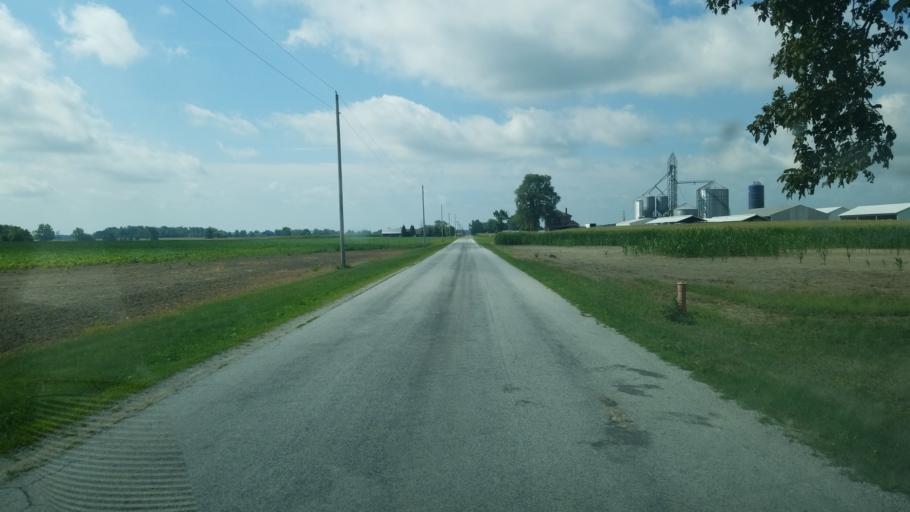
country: US
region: Ohio
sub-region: Hardin County
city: Kenton
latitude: 40.6017
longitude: -83.4438
